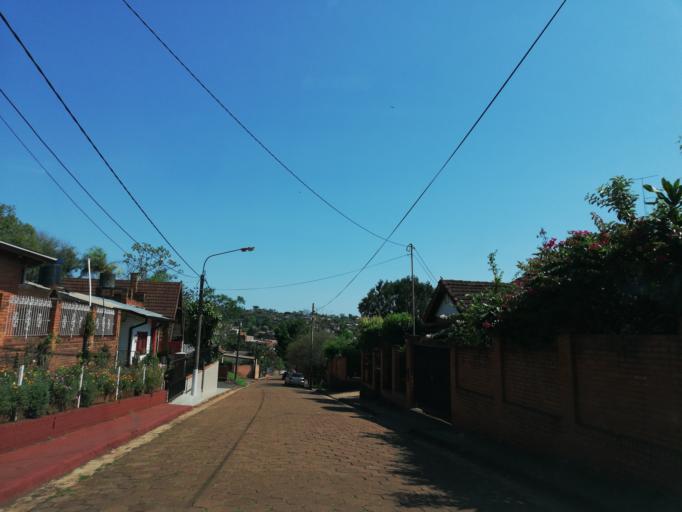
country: AR
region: Misiones
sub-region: Departamento de Eldorado
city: Eldorado
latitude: -26.4084
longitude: -54.6115
